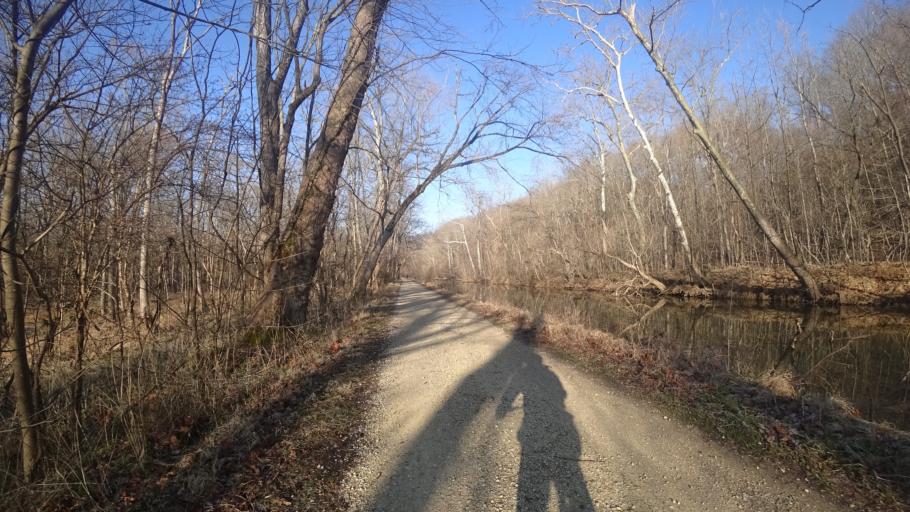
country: US
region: Maryland
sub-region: Montgomery County
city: Travilah
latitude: 39.0596
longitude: -77.3061
